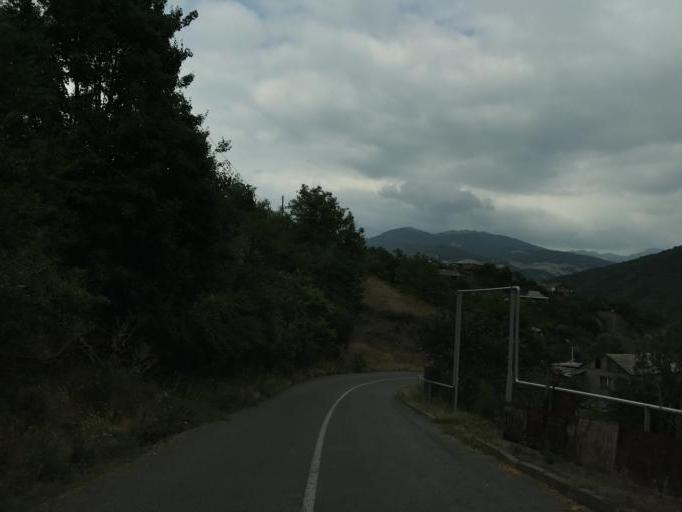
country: AM
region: Tavush
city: Haghartsin
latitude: 40.7310
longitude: 45.0029
